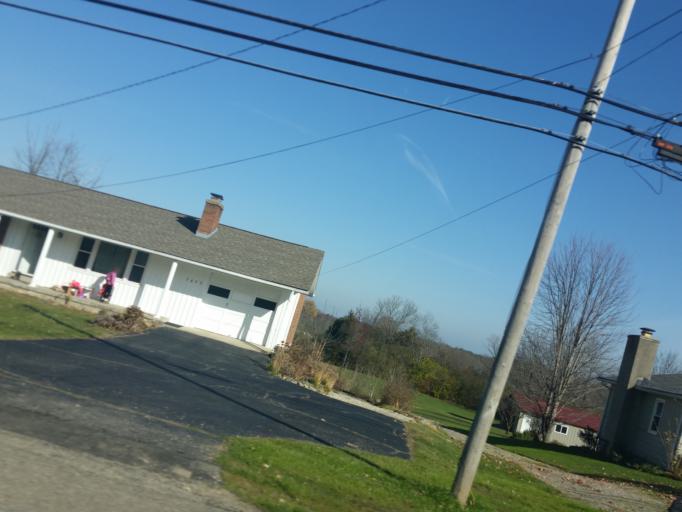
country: US
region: Ohio
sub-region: Butler County
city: Oxford
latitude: 39.4795
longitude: -84.7124
